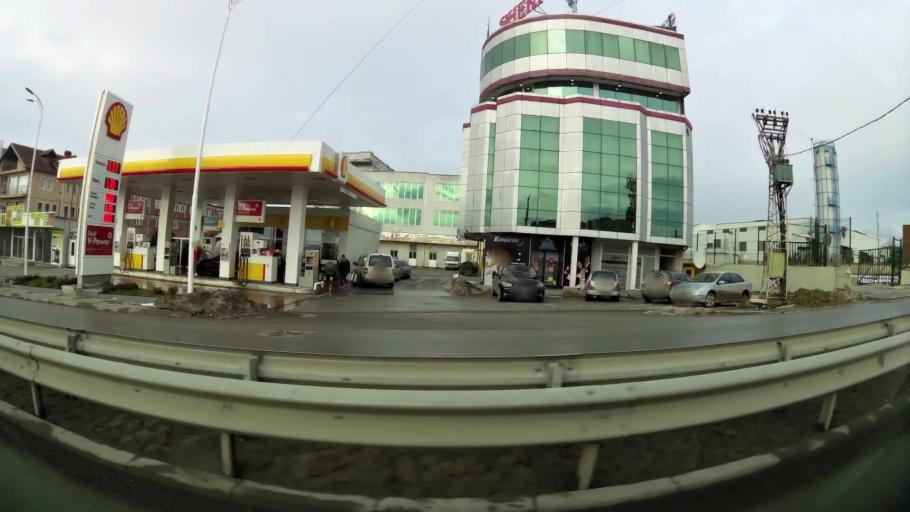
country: XK
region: Pristina
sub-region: Komuna e Prishtines
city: Pristina
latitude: 42.6305
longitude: 21.1534
